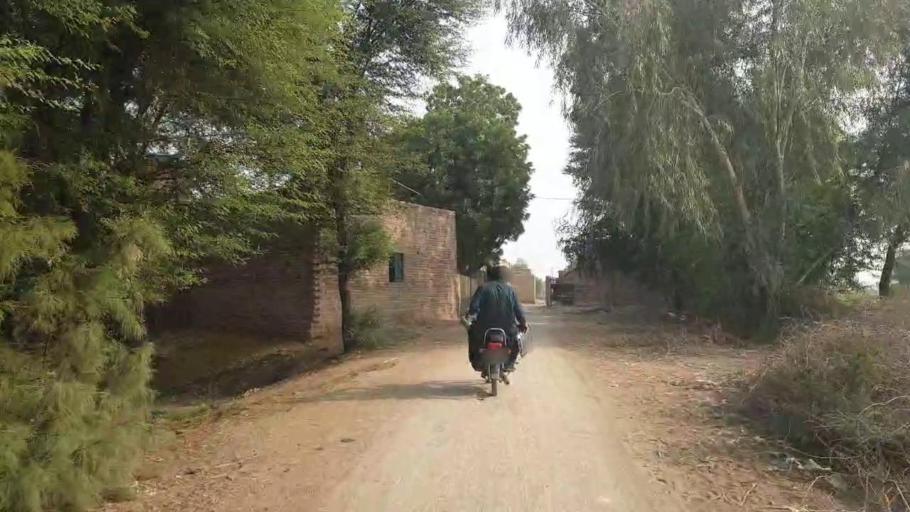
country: PK
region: Sindh
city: Sann
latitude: 26.0699
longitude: 68.1156
